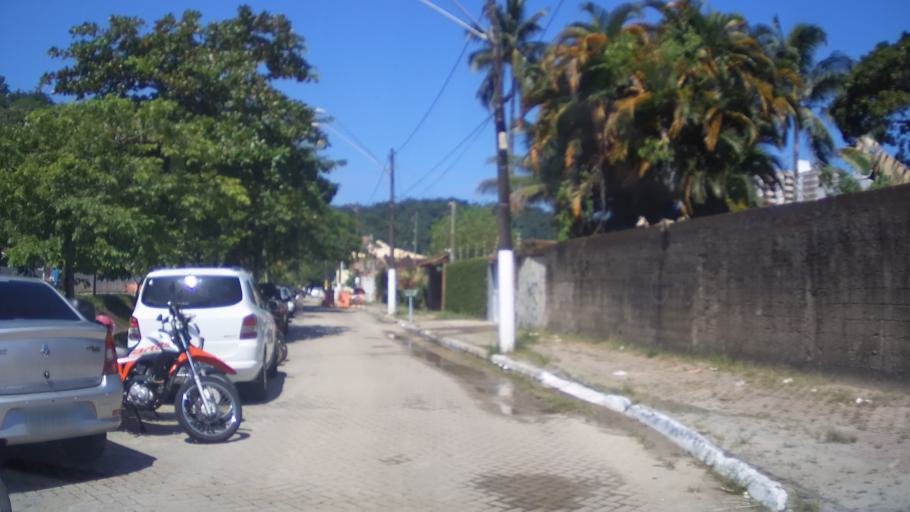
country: BR
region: Sao Paulo
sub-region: Praia Grande
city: Praia Grande
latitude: -24.0080
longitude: -46.3972
